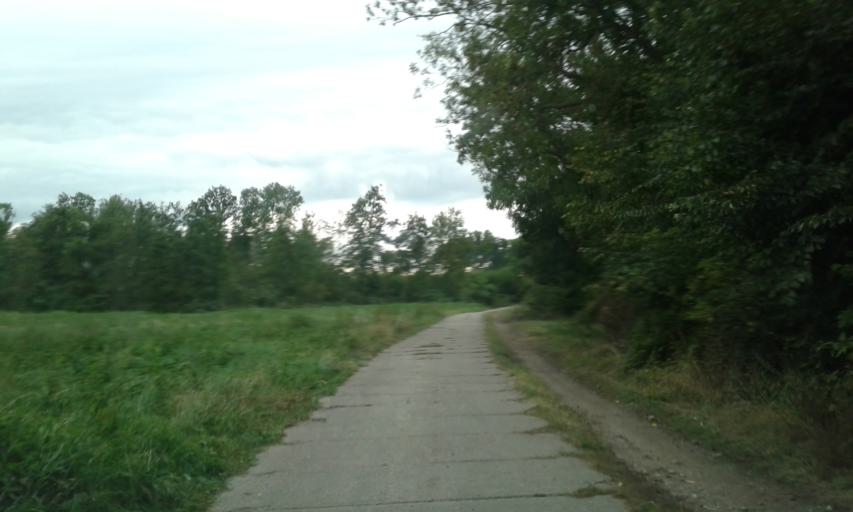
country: PL
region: West Pomeranian Voivodeship
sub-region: Powiat pyrzycki
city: Warnice
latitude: 53.1784
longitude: 14.9977
